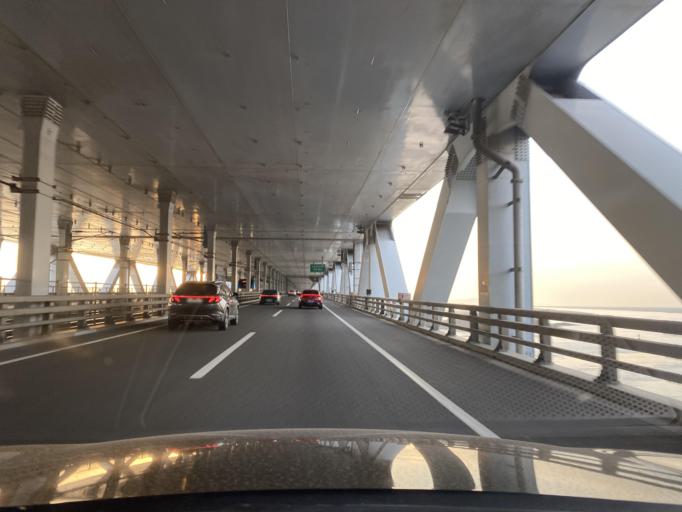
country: KR
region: Gyeonggi-do
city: Tongjin
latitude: 37.5468
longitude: 126.5878
